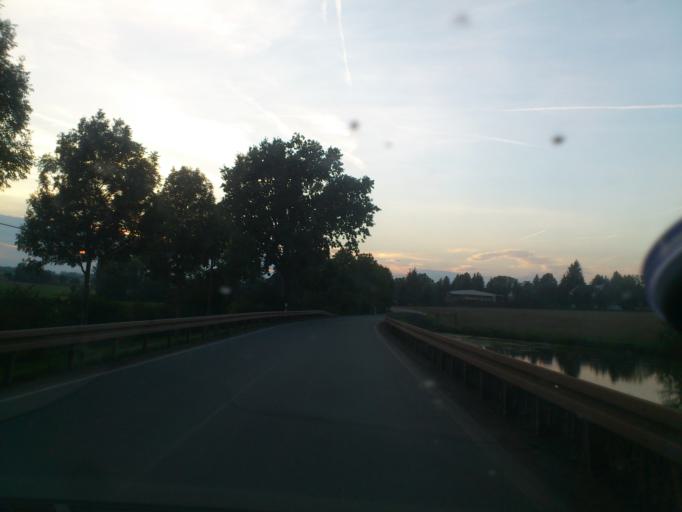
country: DE
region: Saxony
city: Jahnsdorf
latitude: 50.7609
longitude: 12.8441
